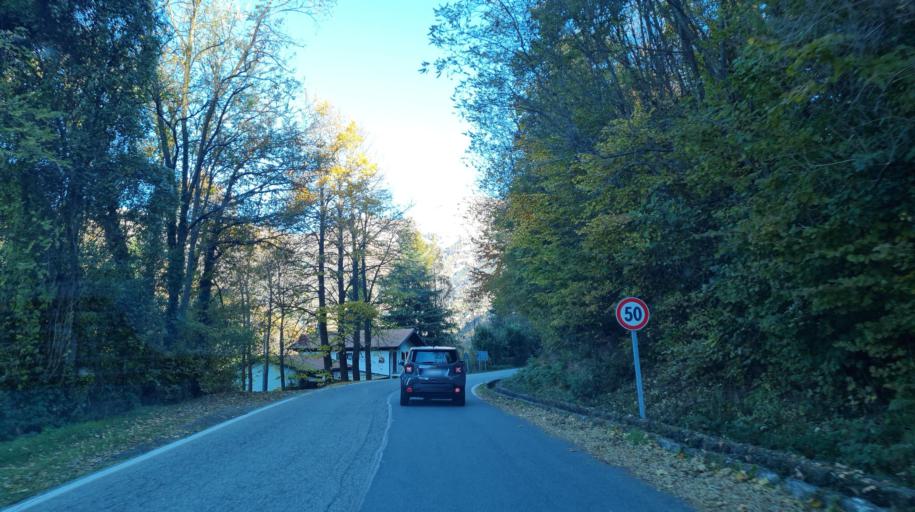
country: IT
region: Piedmont
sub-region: Provincia di Torino
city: Alice Superiore
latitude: 45.4723
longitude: 7.7816
